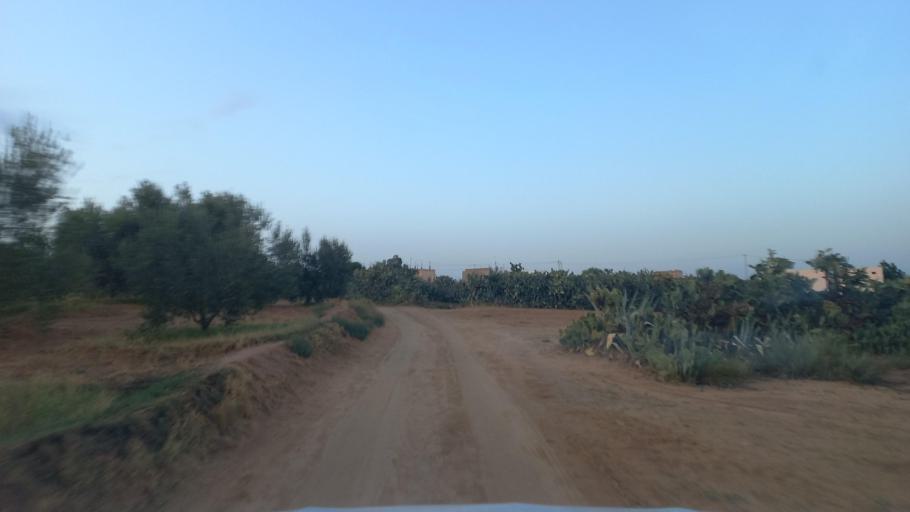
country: TN
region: Al Qasrayn
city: Kasserine
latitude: 35.2188
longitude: 9.0525
